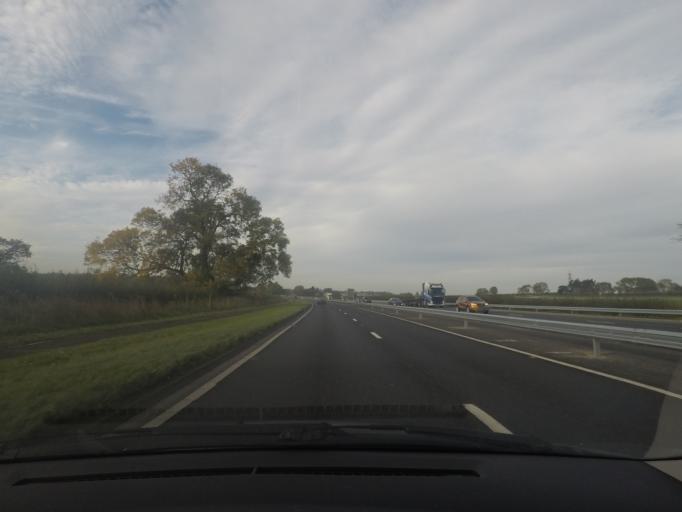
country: GB
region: England
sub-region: City of York
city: Askham Richard
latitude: 53.9171
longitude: -1.1689
